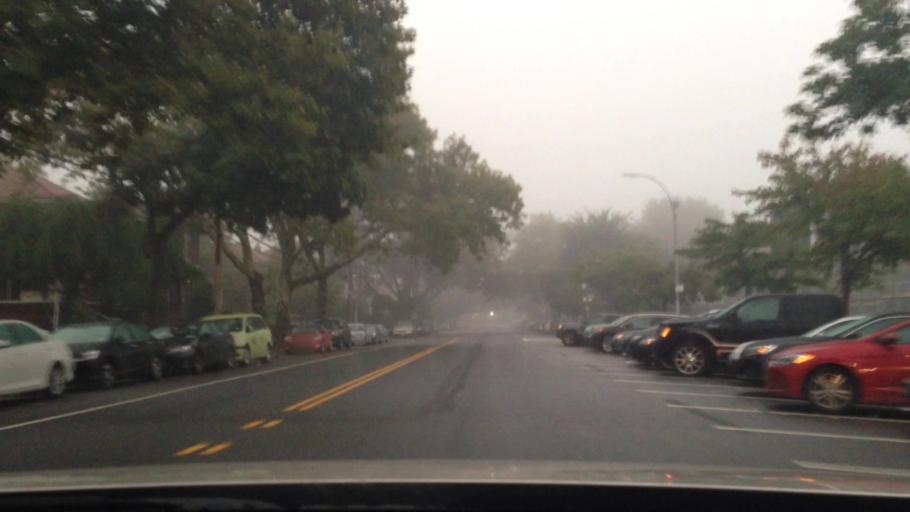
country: US
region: New York
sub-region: Kings County
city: Brooklyn
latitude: 40.6115
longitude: -73.9479
